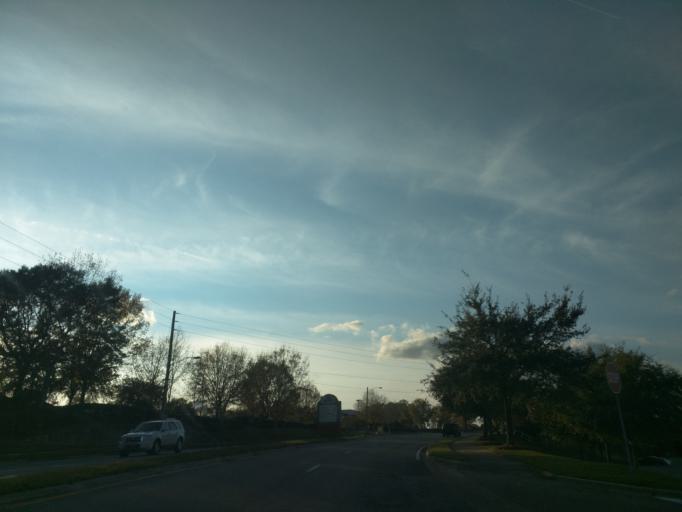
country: US
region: Florida
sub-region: Leon County
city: Tallahassee
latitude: 30.4391
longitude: -84.2570
